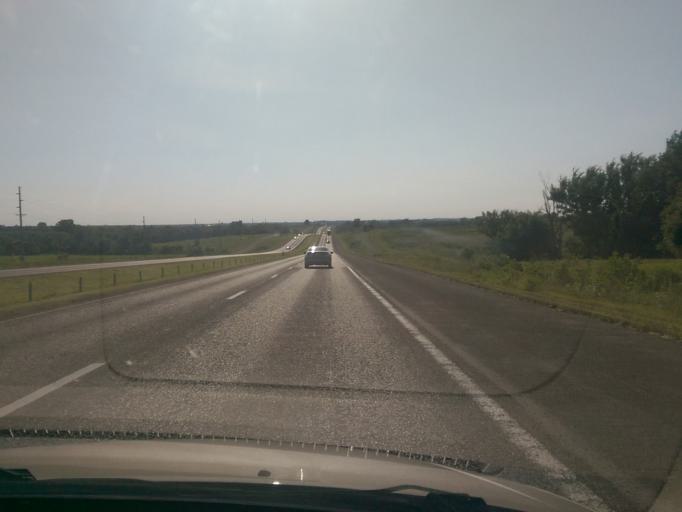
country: US
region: Missouri
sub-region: Lafayette County
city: Higginsville
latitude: 38.9926
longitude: -93.6875
